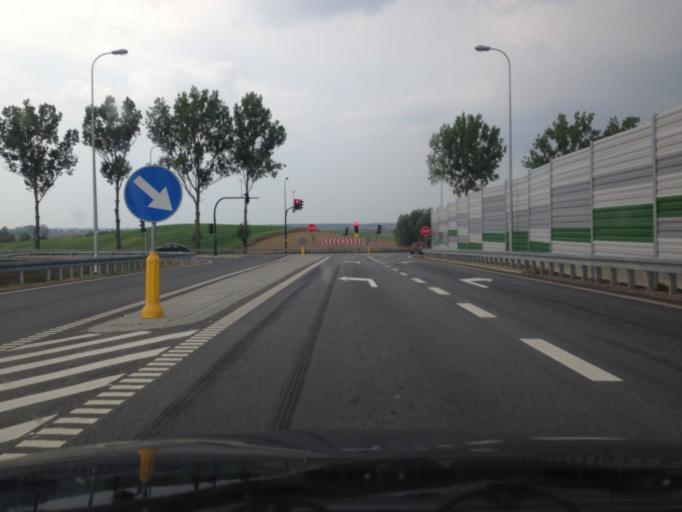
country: PL
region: Pomeranian Voivodeship
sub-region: Powiat tczewski
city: Gniew
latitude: 53.7726
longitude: 18.7721
